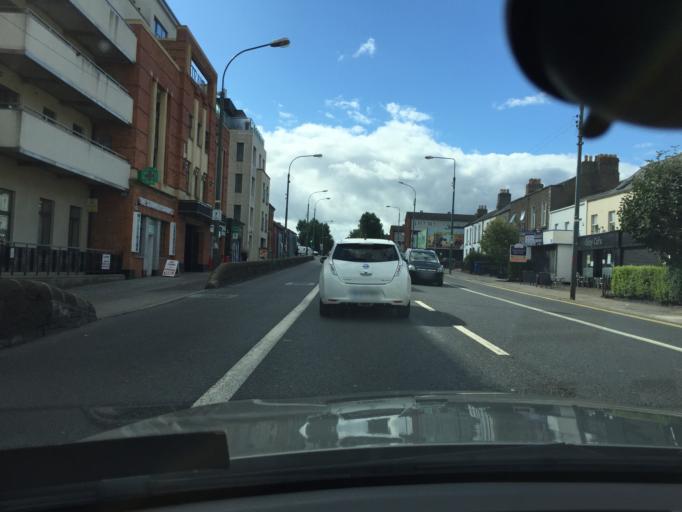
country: IE
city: Fairview
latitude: 53.3574
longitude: -6.2429
